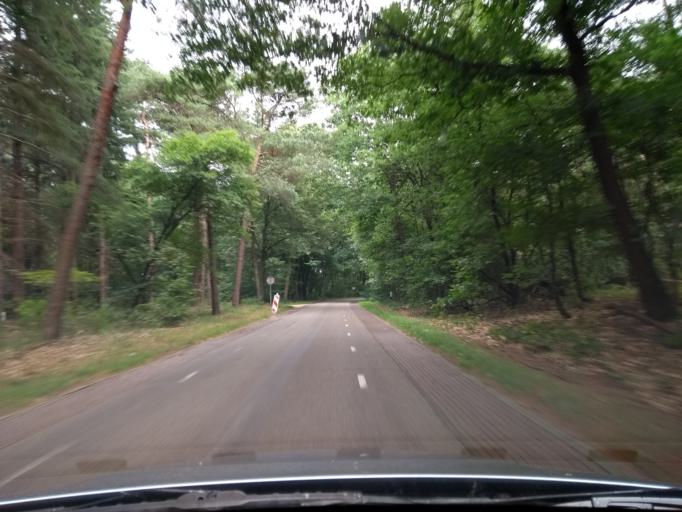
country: NL
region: Overijssel
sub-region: Gemeente Twenterand
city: Den Ham
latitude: 52.4575
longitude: 6.4029
